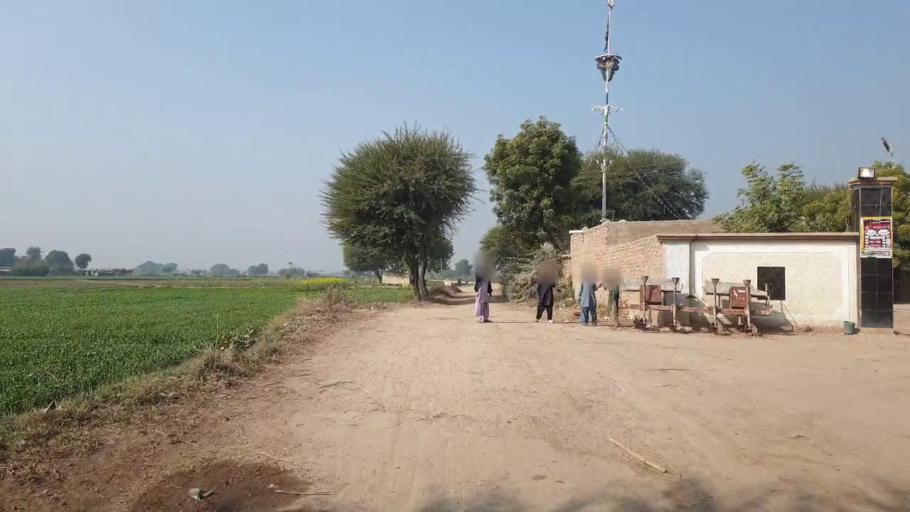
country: PK
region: Sindh
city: Bhit Shah
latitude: 25.7245
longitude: 68.5020
